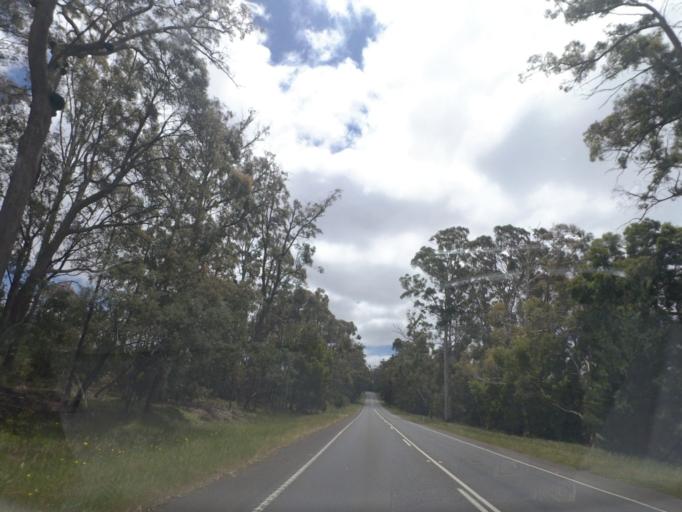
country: AU
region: Victoria
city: Brown Hill
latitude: -37.4888
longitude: 144.1539
